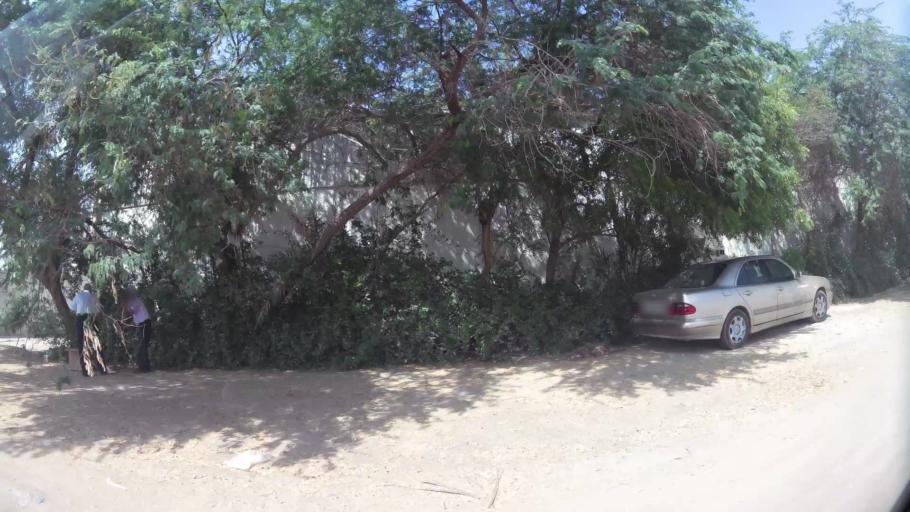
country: AE
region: Ash Shariqah
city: Sharjah
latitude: 25.3089
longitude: 55.3830
